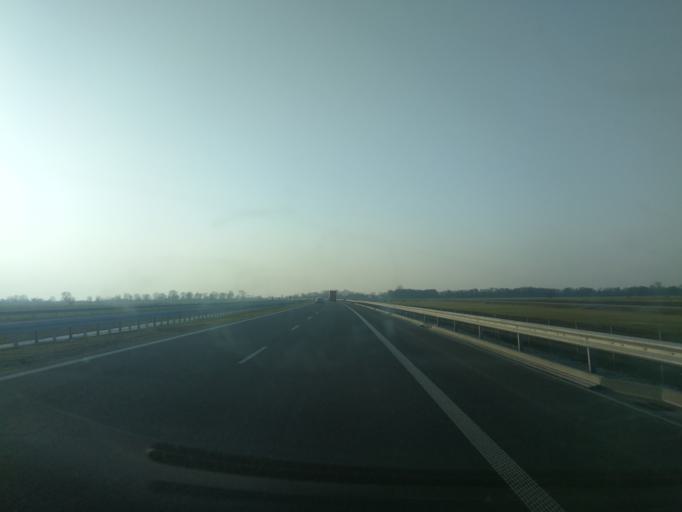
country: PL
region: Pomeranian Voivodeship
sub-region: Powiat nowodworski
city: Nowy Dwor Gdanski
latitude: 54.1707
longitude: 19.2214
